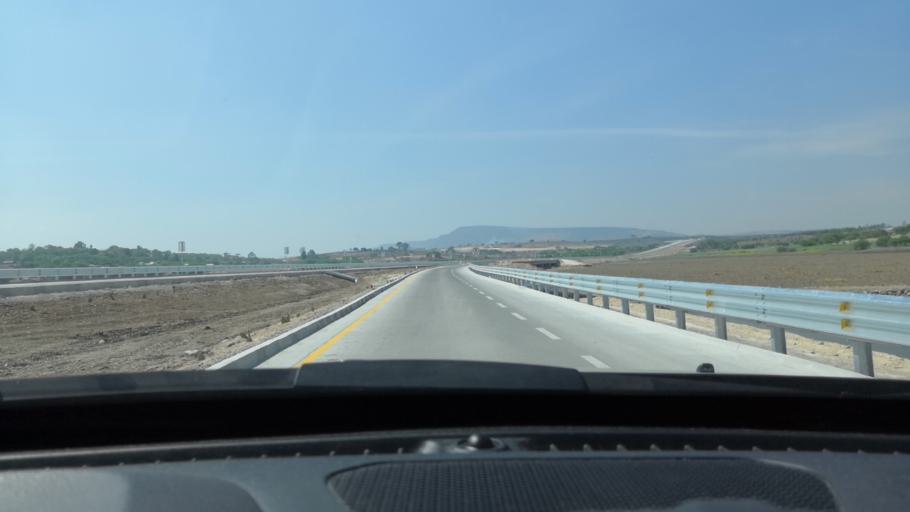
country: MX
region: Guanajuato
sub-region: Purisima del Rincon
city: Potrerillos (Guanajal)
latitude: 21.0761
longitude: -101.8621
